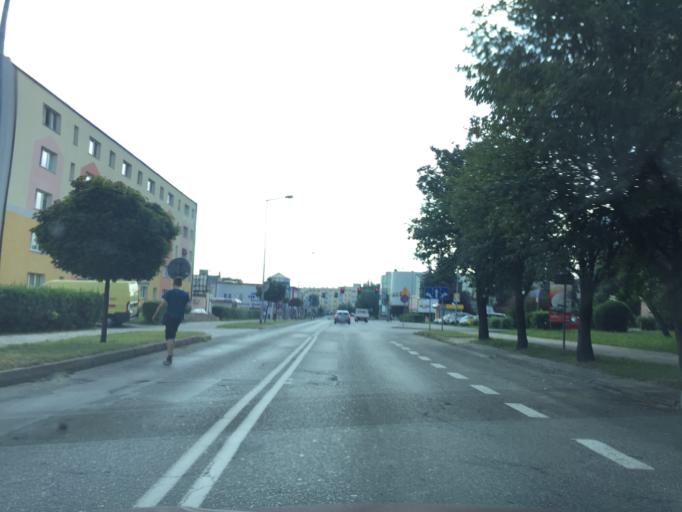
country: PL
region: Greater Poland Voivodeship
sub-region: Kalisz
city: Kalisz
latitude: 51.7482
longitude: 18.0709
